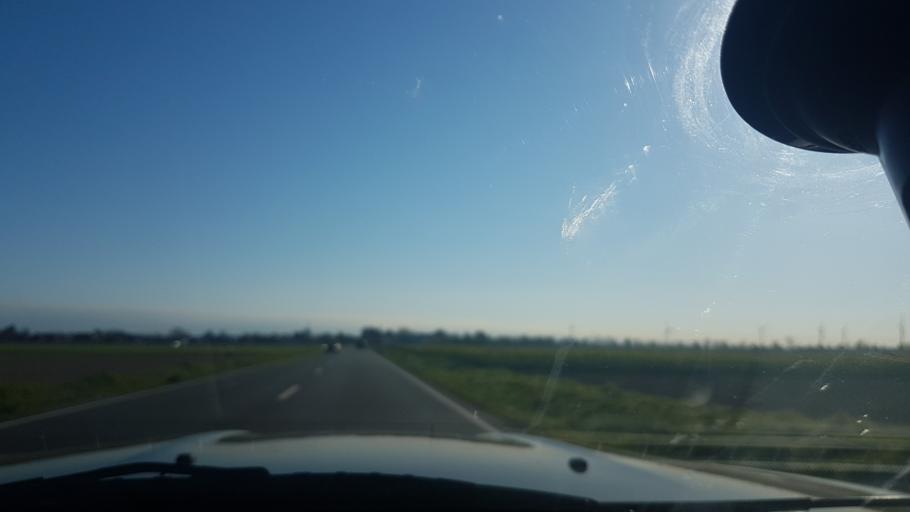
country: DE
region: Lower Saxony
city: Hemmingen
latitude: 52.2743
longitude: 9.6938
